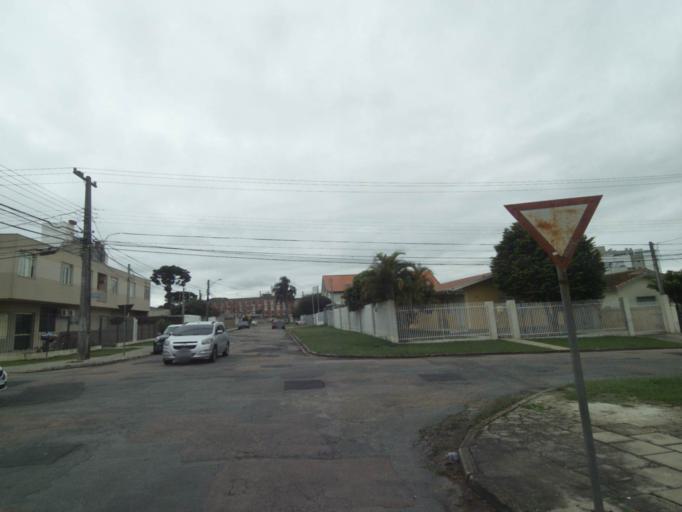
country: BR
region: Parana
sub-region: Curitiba
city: Curitiba
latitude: -25.4846
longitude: -49.2905
